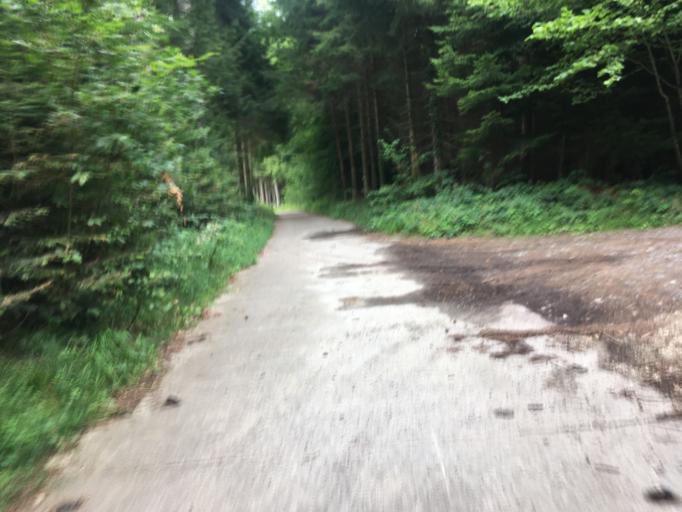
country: CH
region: Fribourg
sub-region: Broye District
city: Estavayer-le-Lac
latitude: 46.8709
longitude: 6.8958
